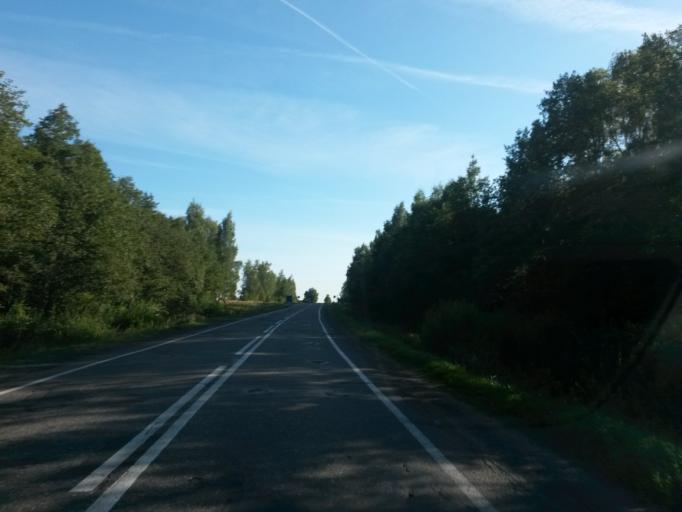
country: RU
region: Jaroslavl
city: Gavrilov-Yam
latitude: 57.3812
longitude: 39.9103
